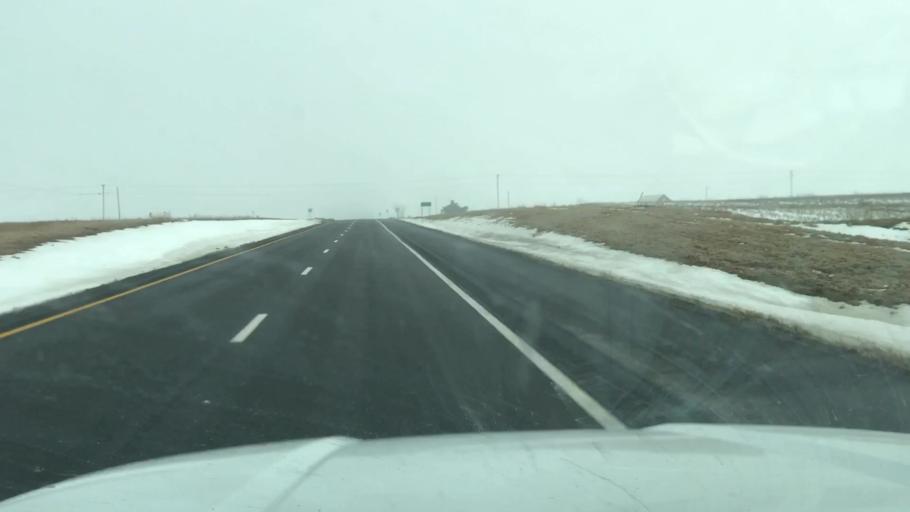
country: US
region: Missouri
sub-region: DeKalb County
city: Maysville
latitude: 39.7621
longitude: -94.4347
